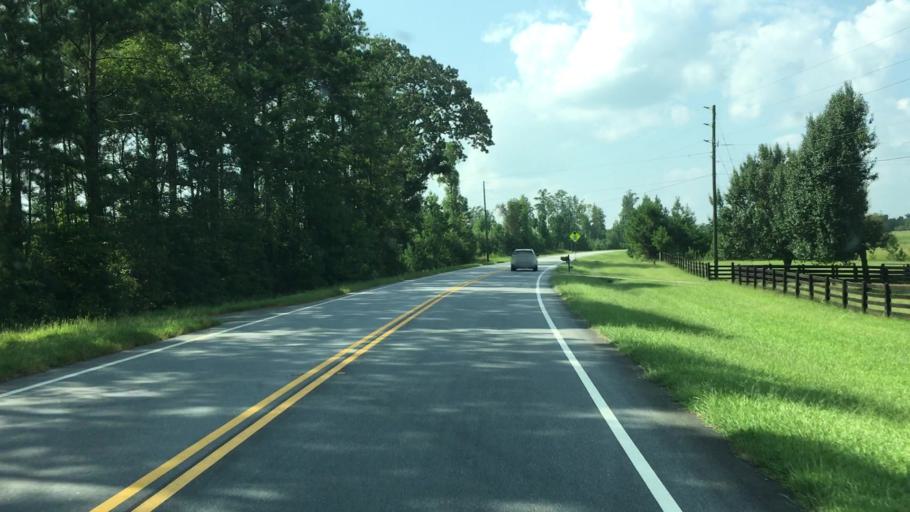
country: US
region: Georgia
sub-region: Jasper County
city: Monticello
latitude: 33.3307
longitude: -83.7095
